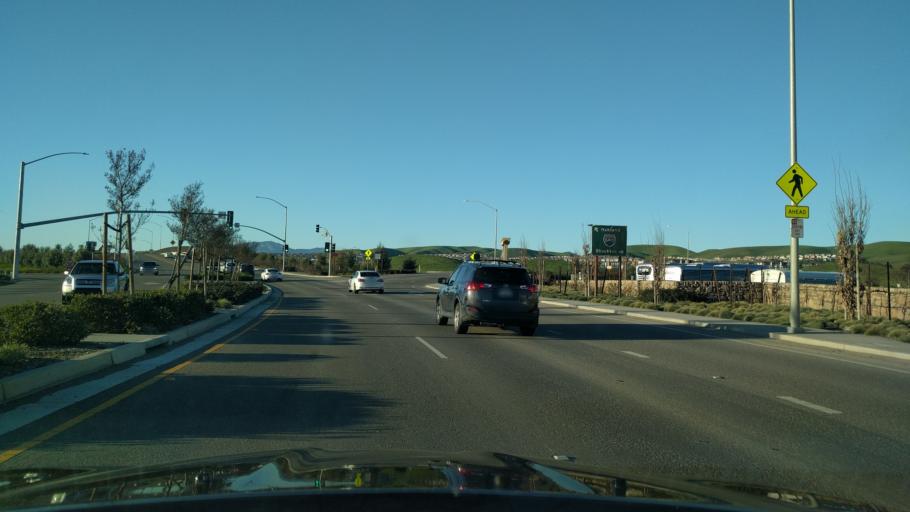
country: US
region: California
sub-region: Alameda County
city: Pleasanton
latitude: 37.6990
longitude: -121.8481
